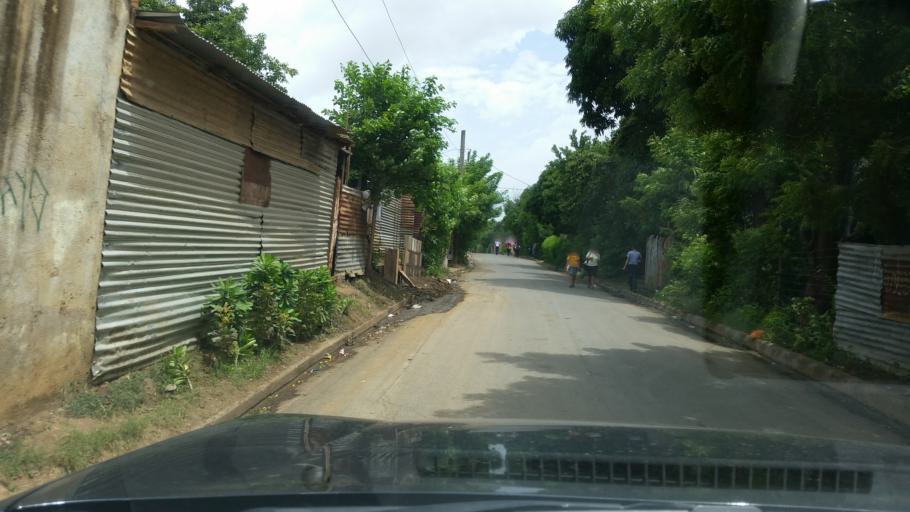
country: NI
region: Managua
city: Managua
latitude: 12.1117
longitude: -86.2166
